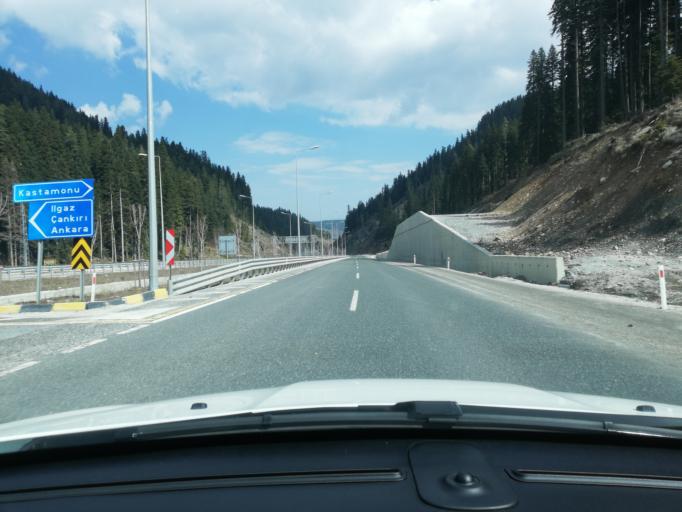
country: TR
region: Kastamonu
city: Kuzyaka
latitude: 41.0898
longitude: 33.7492
